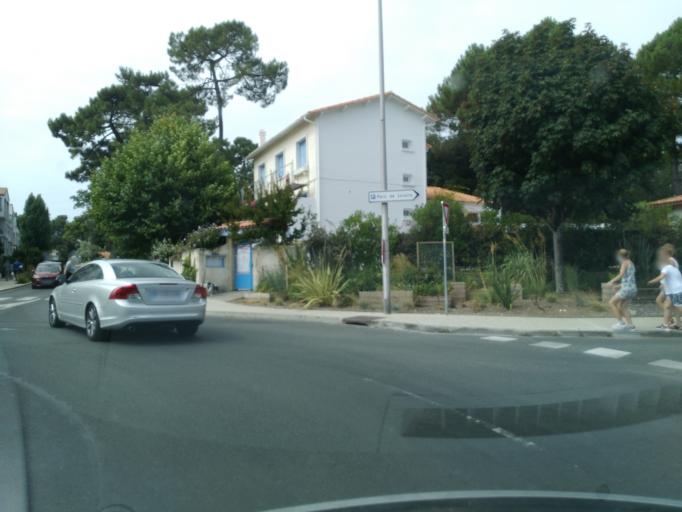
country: FR
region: Poitou-Charentes
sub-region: Departement de la Charente-Maritime
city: Saint-Palais-sur-Mer
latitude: 45.6457
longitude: -1.0902
